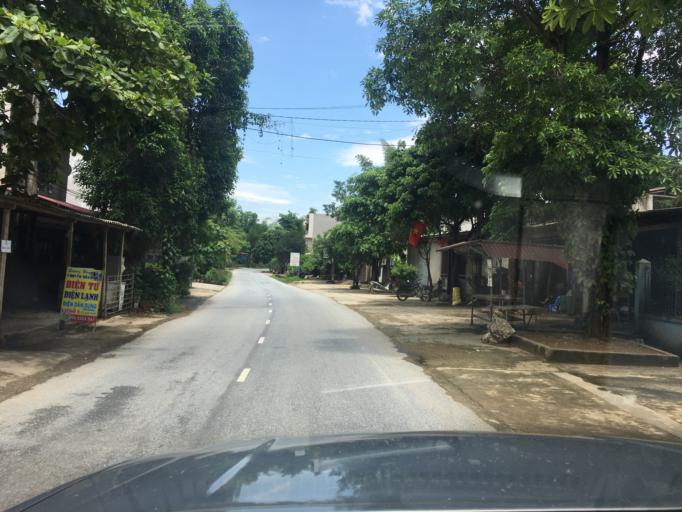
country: VN
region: Yen Bai
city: Son Thinh
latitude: 21.6555
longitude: 104.4998
